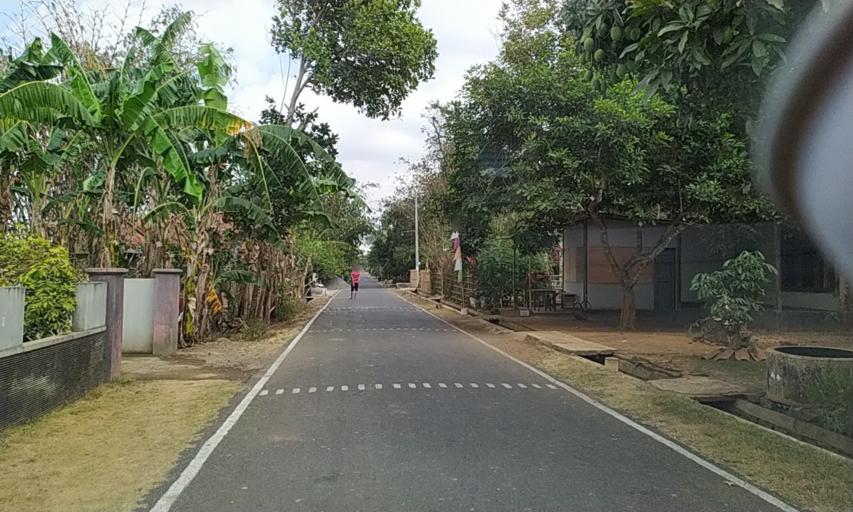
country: ID
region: Central Java
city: Kroya
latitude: -7.6353
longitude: 109.2619
